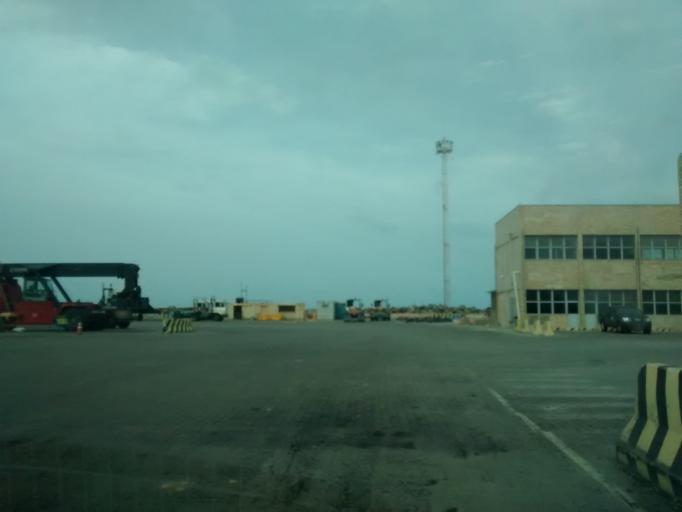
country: BR
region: Ceara
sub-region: Caucaia
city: Cambebba
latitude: -3.5314
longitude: -38.7936
